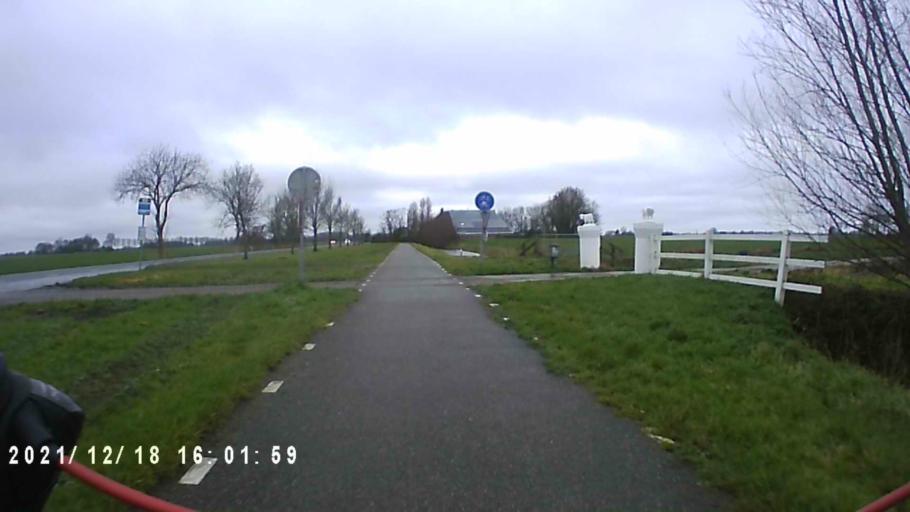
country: NL
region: Friesland
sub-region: Gemeente Dongeradeel
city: Anjum
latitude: 53.3462
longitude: 6.0848
